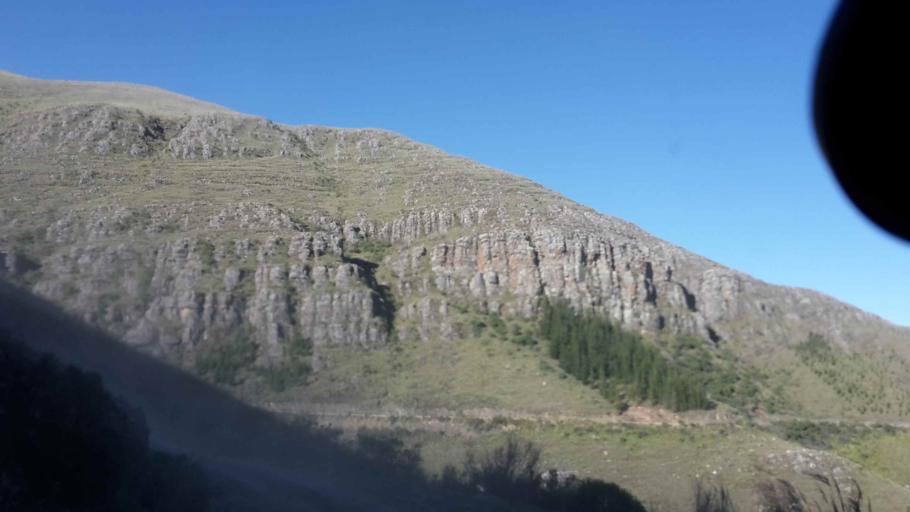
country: BO
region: Cochabamba
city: Arani
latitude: -17.7234
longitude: -65.6460
